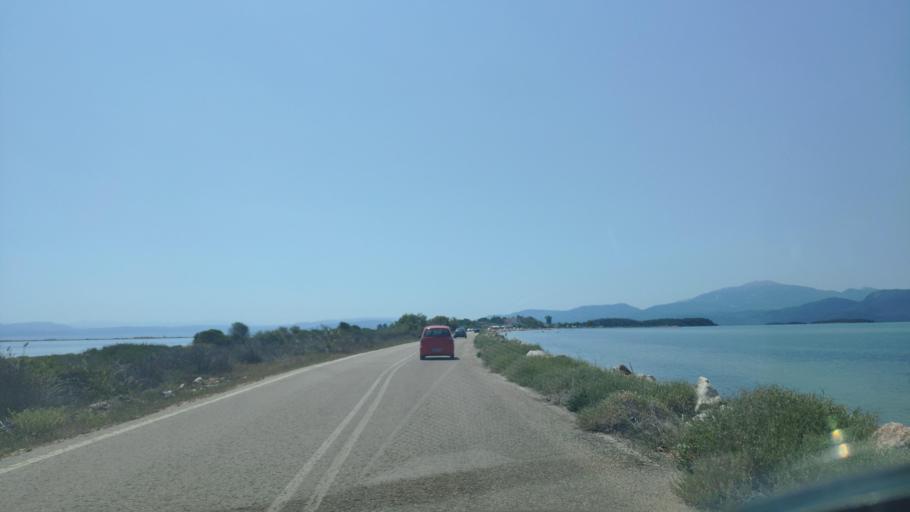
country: GR
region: Epirus
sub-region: Nomos Artas
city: Aneza
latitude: 39.0258
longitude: 20.9068
